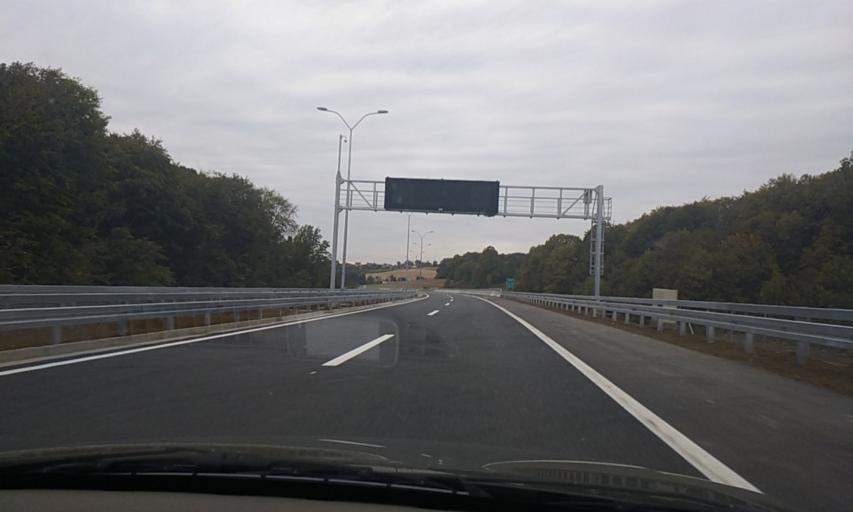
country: BA
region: Republika Srpska
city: Prnjavor
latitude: 44.8694
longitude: 17.5067
